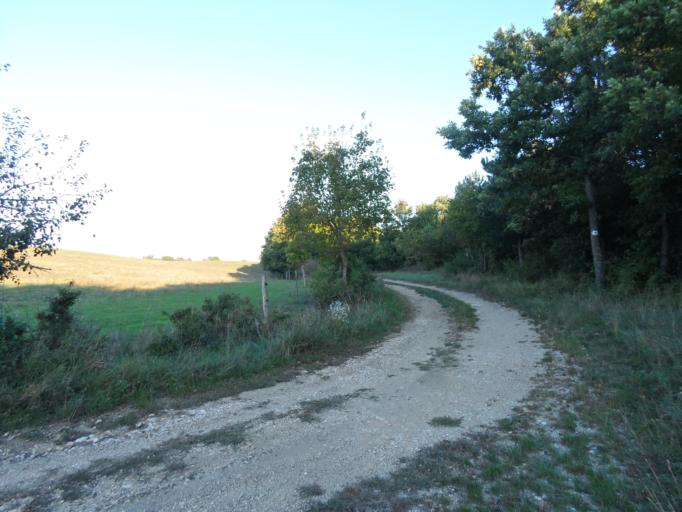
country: HU
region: Veszprem
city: Papa
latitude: 47.2386
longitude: 17.5561
